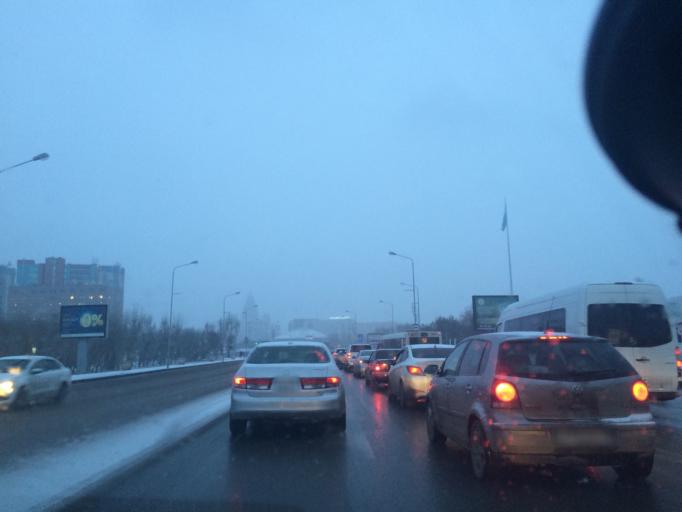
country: KZ
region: Astana Qalasy
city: Astana
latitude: 51.1505
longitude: 71.4261
